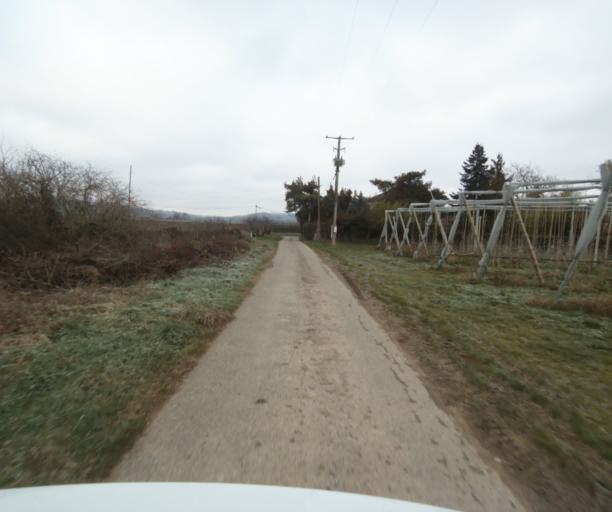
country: FR
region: Midi-Pyrenees
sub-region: Departement du Tarn-et-Garonne
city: Moissac
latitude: 44.1073
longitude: 1.1338
